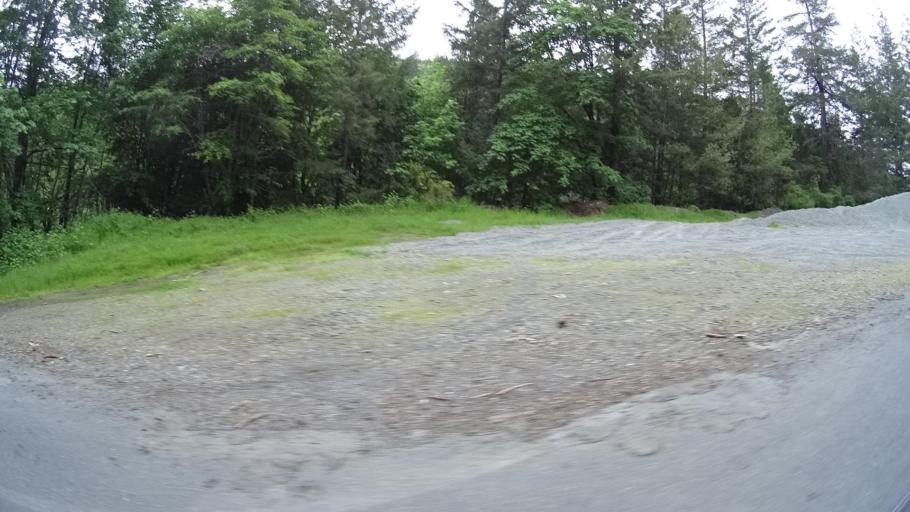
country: US
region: California
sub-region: Humboldt County
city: Willow Creek
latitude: 41.2057
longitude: -123.7568
